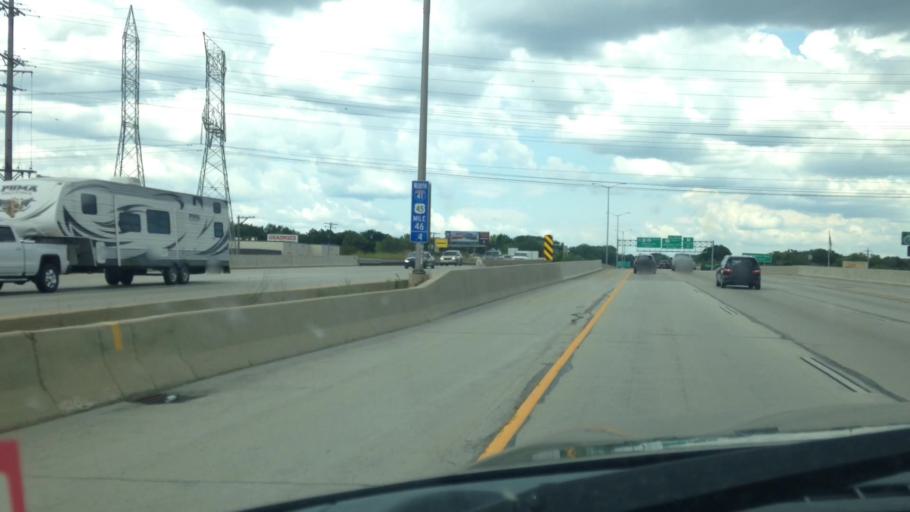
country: US
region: Wisconsin
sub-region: Waukesha County
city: Butler
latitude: 43.1200
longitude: -88.0571
